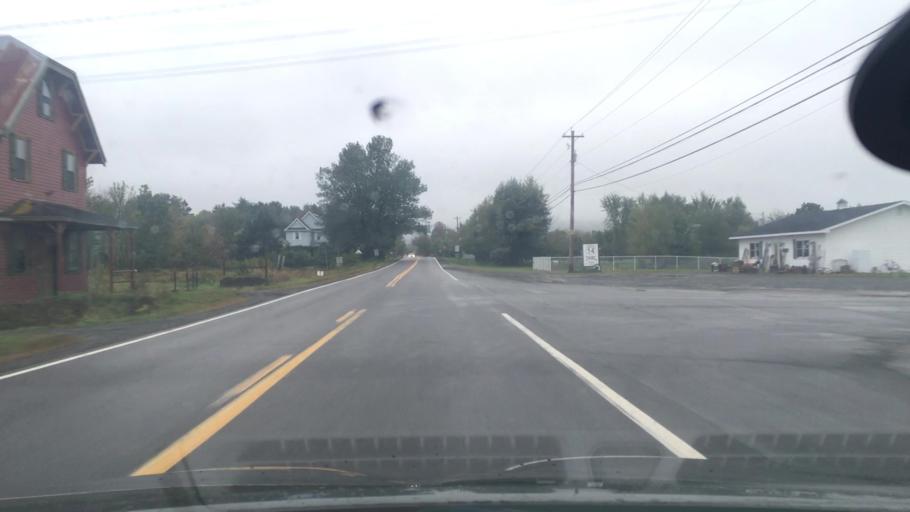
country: CA
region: Nova Scotia
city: Windsor
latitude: 44.9416
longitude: -64.1869
